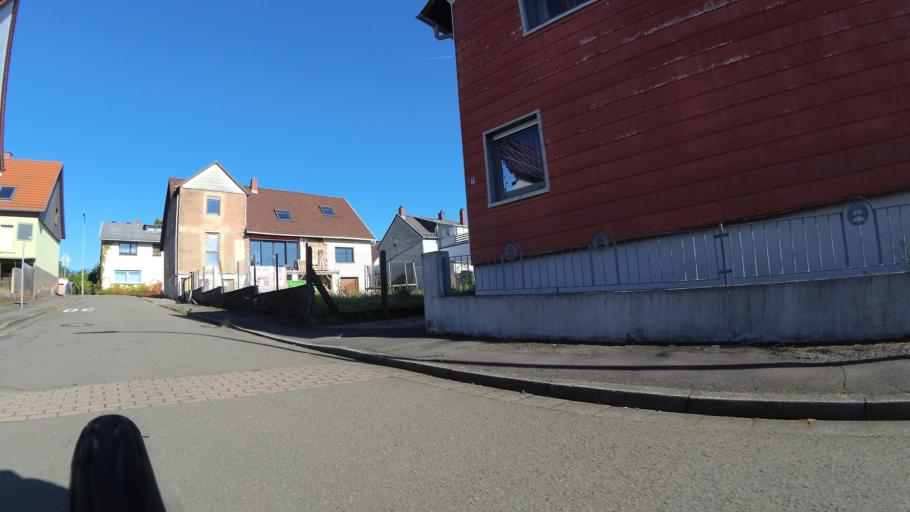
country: DE
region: Rheinland-Pfalz
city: Waldmohr
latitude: 49.3847
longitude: 7.3364
